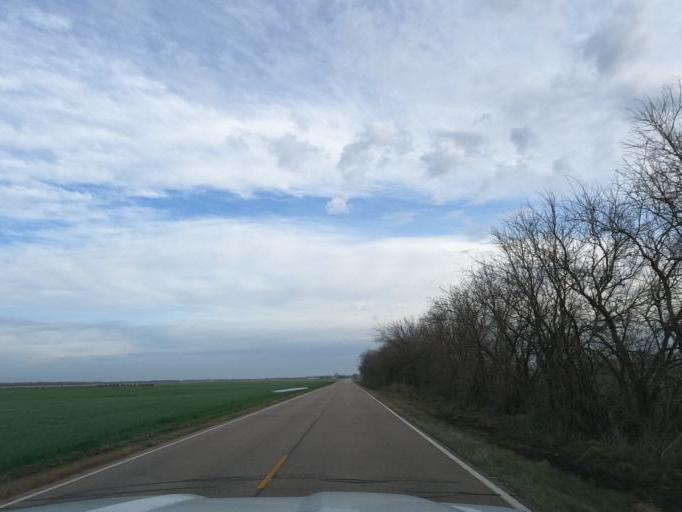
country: US
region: Kansas
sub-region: Reno County
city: Nickerson
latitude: 37.9904
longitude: -98.1786
